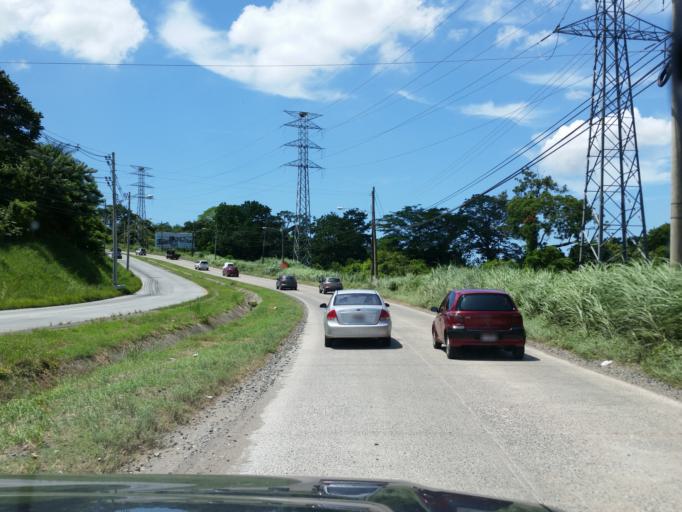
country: PA
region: Panama
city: San Miguelito
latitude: 9.0677
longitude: -79.4629
